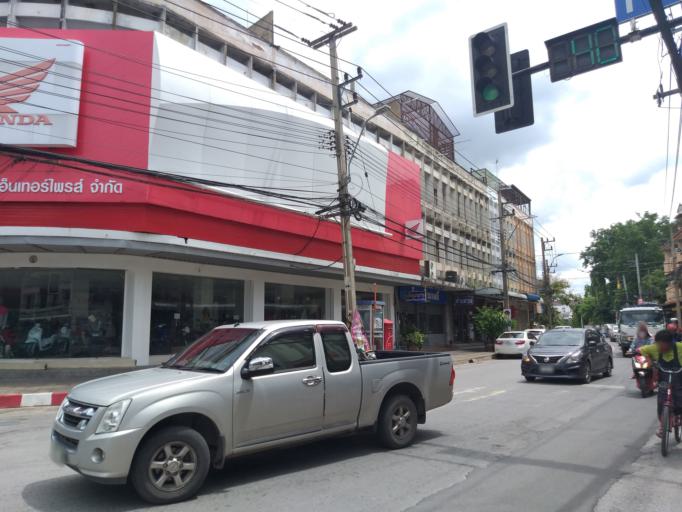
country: TH
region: Nakhon Ratchasima
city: Nakhon Ratchasima
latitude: 14.9769
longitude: 102.0909
